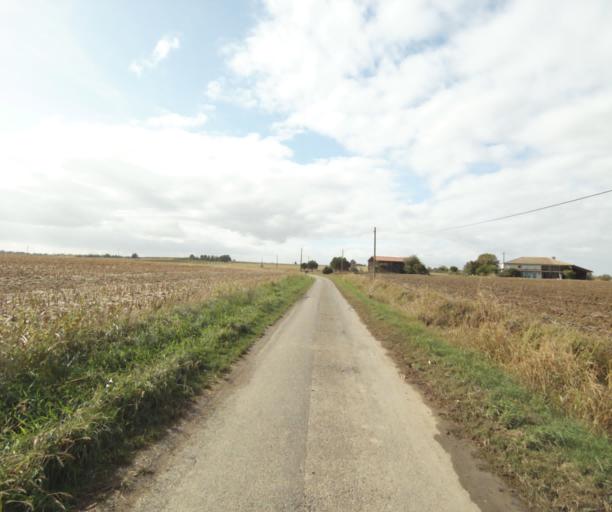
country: FR
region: Midi-Pyrenees
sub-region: Departement du Tarn-et-Garonne
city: Finhan
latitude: 43.9037
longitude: 1.1616
